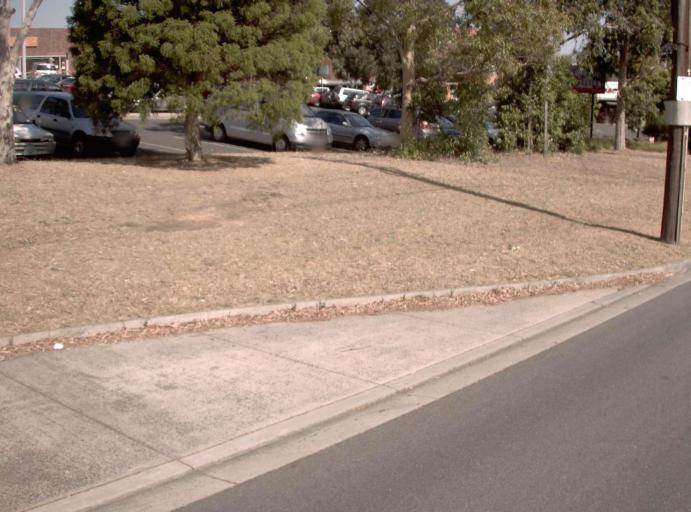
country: AU
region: Victoria
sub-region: Monash
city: Mulgrave
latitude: -37.9099
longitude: 145.1885
